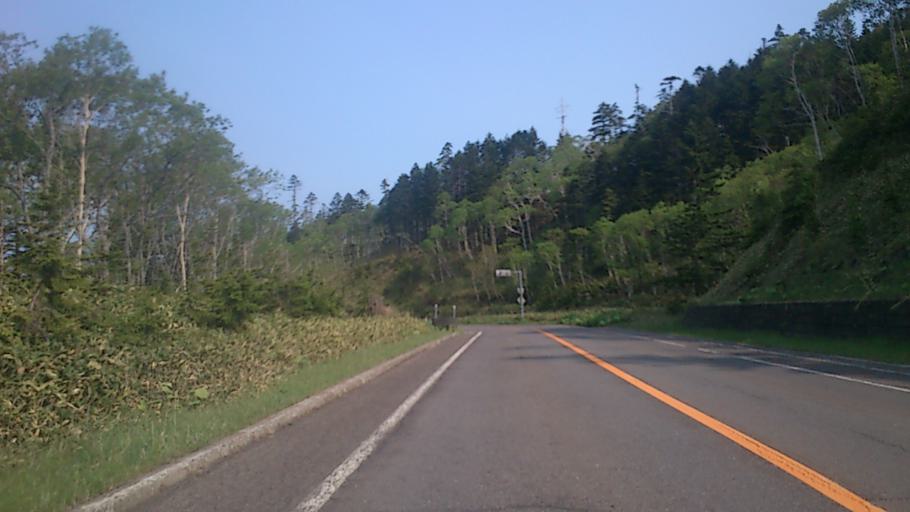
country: JP
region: Hokkaido
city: Bihoro
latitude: 43.4530
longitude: 144.2262
